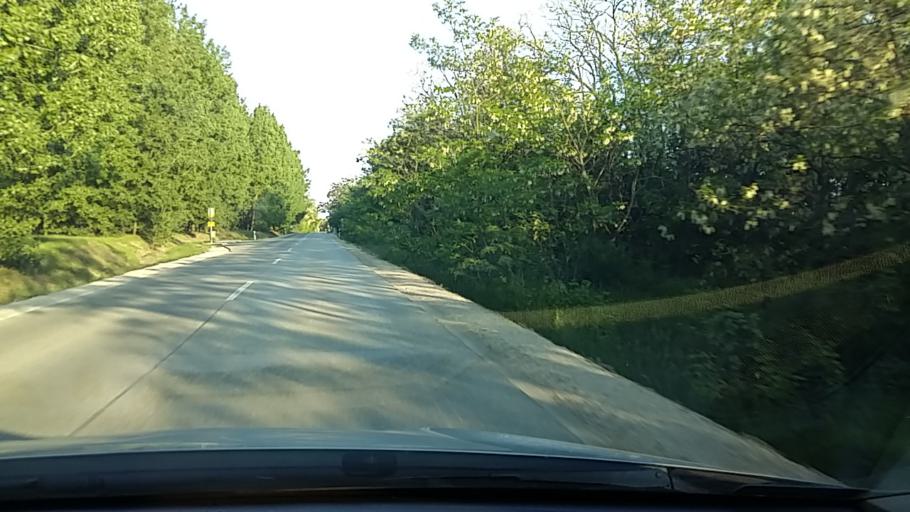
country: HU
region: Pest
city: Orbottyan
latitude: 47.6928
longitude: 19.2532
